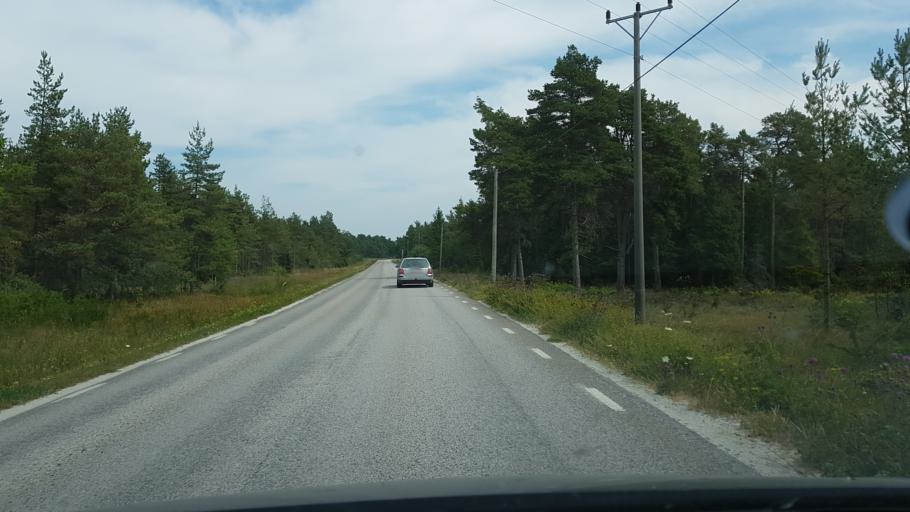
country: SE
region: Gotland
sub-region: Gotland
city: Slite
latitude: 57.7228
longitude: 18.7645
